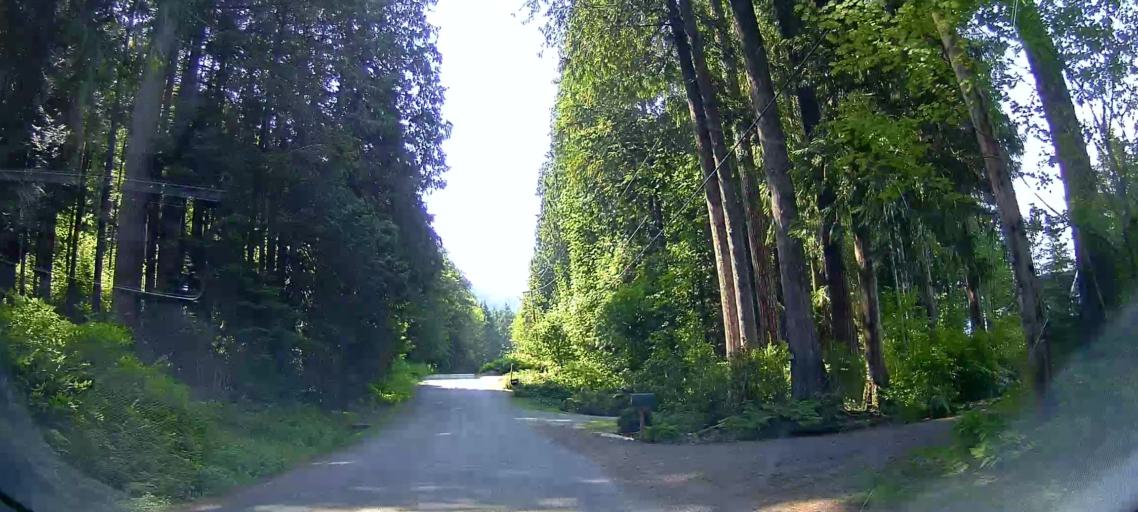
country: US
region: Washington
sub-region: Snohomish County
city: Arlington Heights
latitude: 48.3175
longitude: -122.0177
